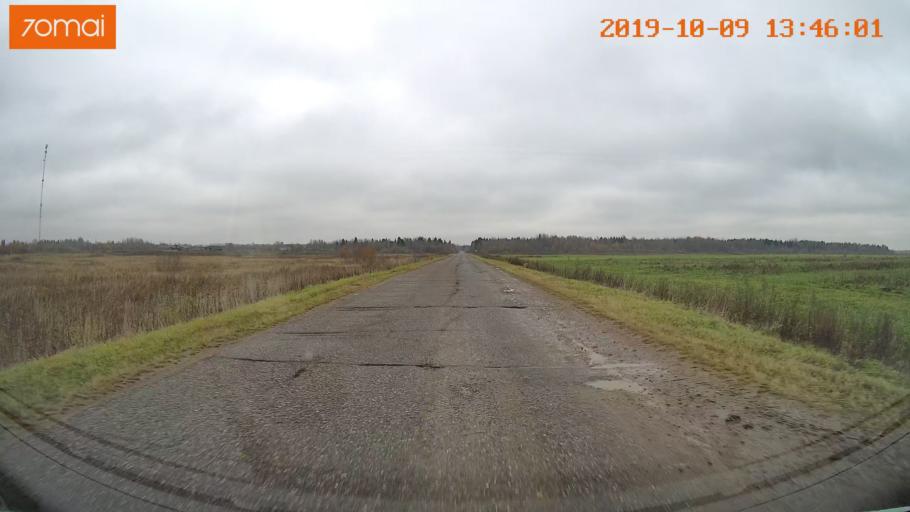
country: RU
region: Kostroma
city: Buy
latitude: 58.3798
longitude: 41.2147
